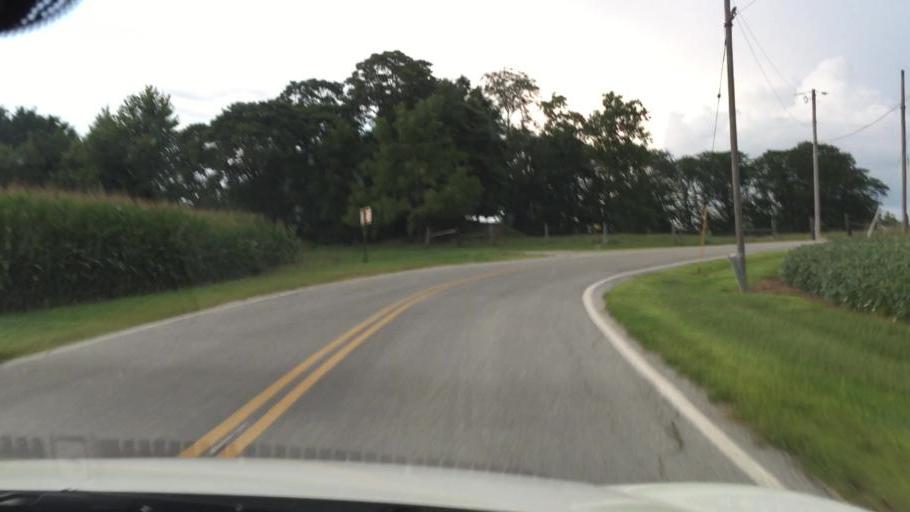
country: US
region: Ohio
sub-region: Champaign County
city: Mechanicsburg
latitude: 39.9959
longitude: -83.6374
